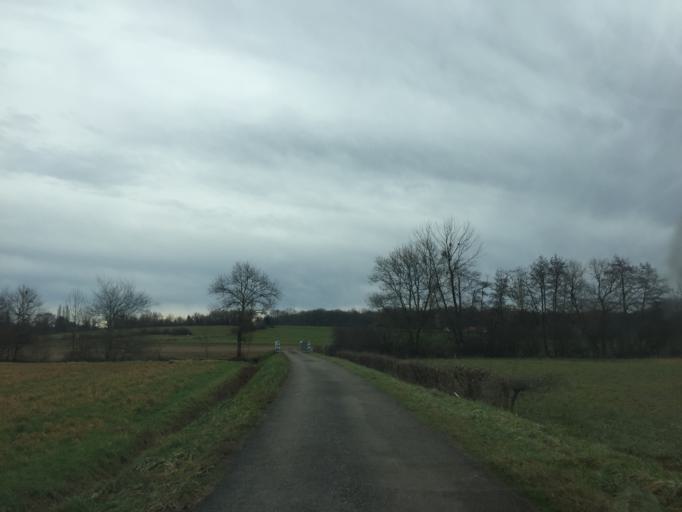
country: FR
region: Franche-Comte
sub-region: Departement du Jura
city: Mont-sous-Vaudrey
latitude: 46.8675
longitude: 5.5227
